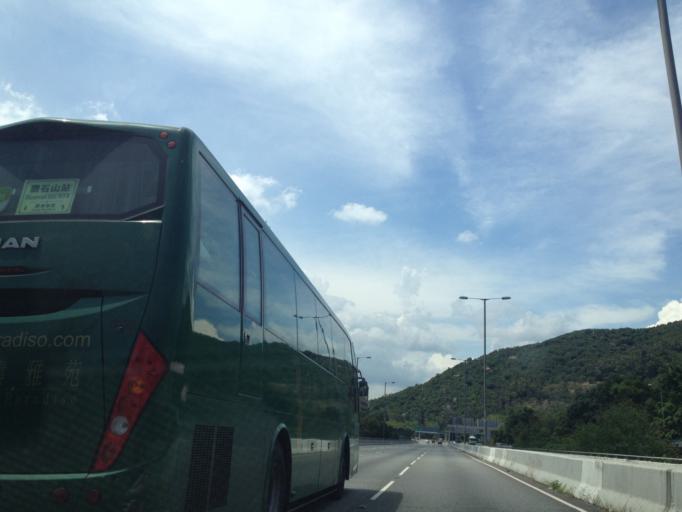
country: HK
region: Sha Tin
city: Sha Tin
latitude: 22.3831
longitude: 114.2104
